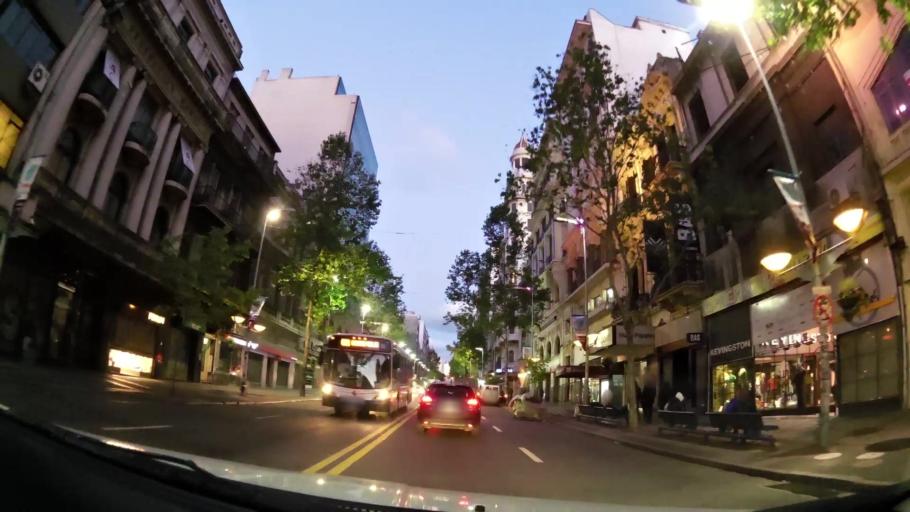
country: UY
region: Montevideo
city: Montevideo
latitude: -34.9063
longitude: -56.1956
